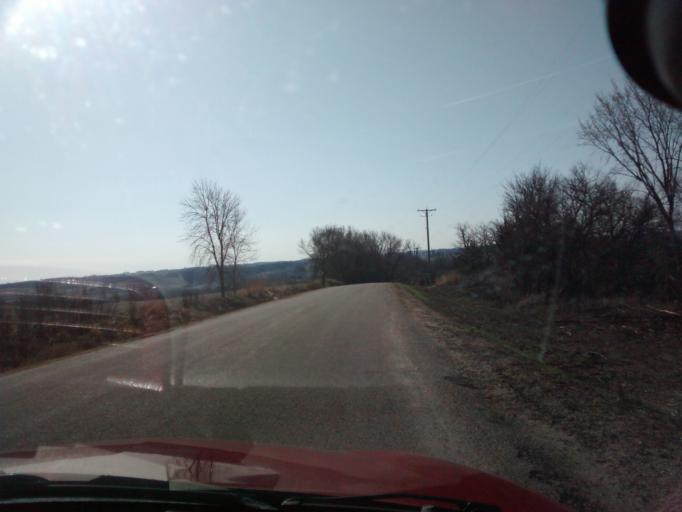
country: US
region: Iowa
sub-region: Pottawattamie County
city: Carter Lake
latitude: 41.4168
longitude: -95.8500
